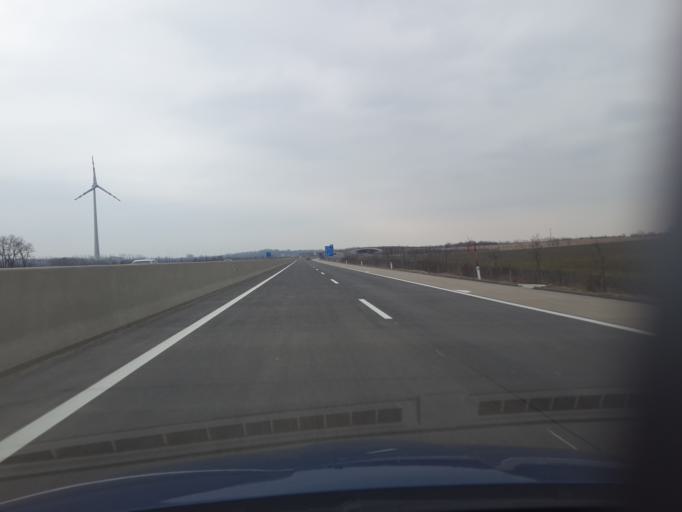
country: AT
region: Burgenland
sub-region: Politischer Bezirk Neusiedl am See
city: Gattendorf
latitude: 48.0468
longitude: 16.9937
